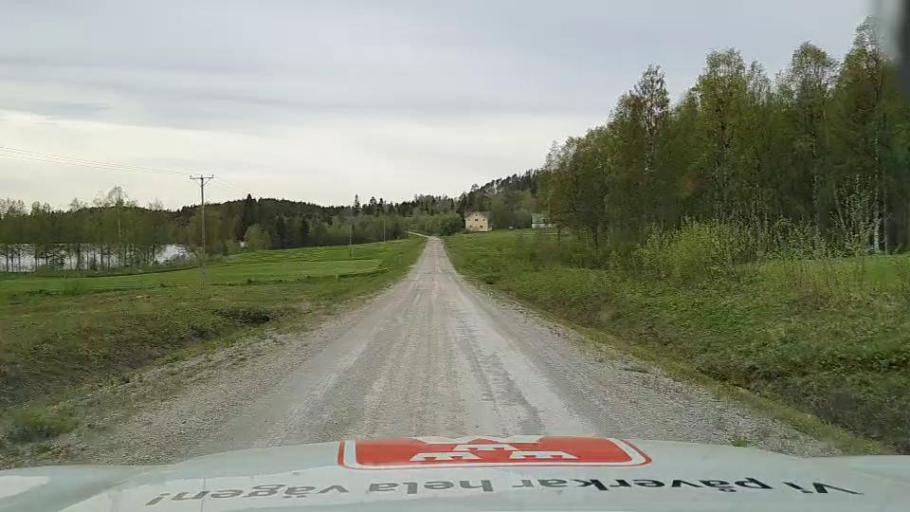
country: SE
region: Jaemtland
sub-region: Bergs Kommun
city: Hoverberg
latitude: 62.6660
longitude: 14.8202
